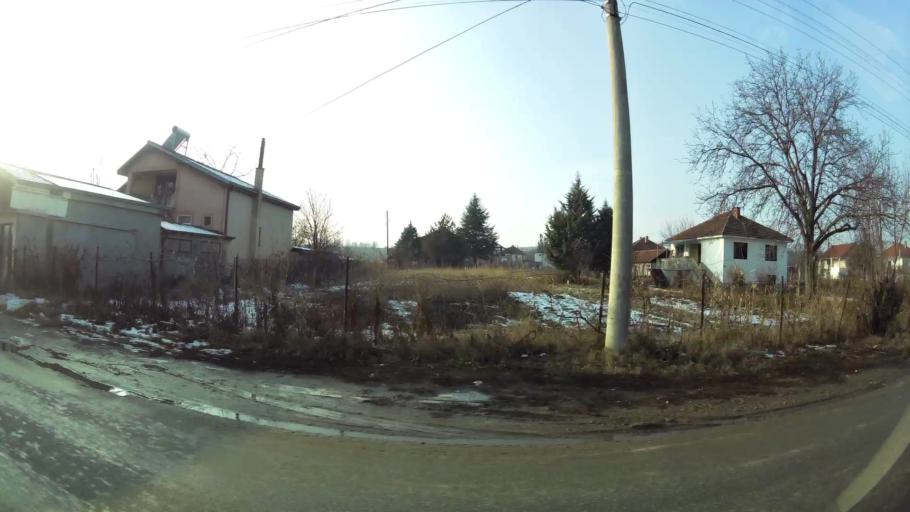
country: MK
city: Miladinovci
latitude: 41.9852
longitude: 21.6511
